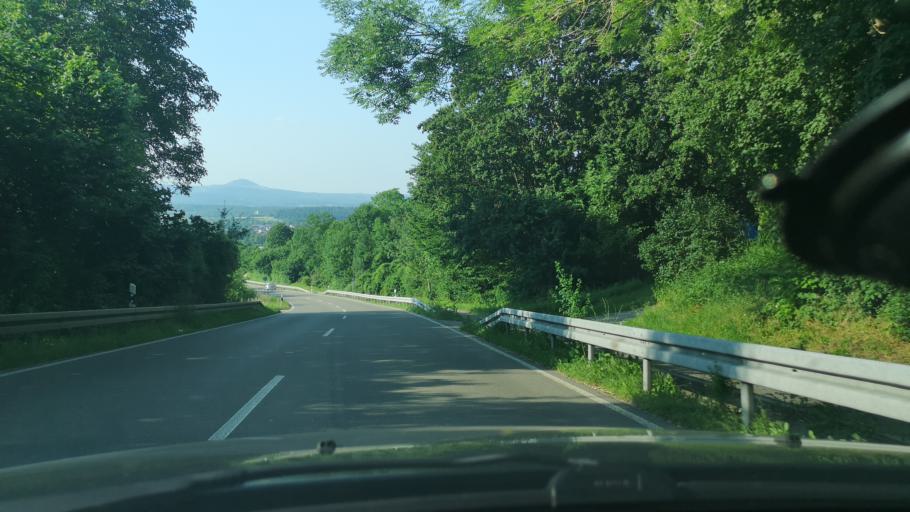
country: DE
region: Baden-Wuerttemberg
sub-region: Regierungsbezirk Stuttgart
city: Schlat
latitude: 48.6406
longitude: 9.7024
